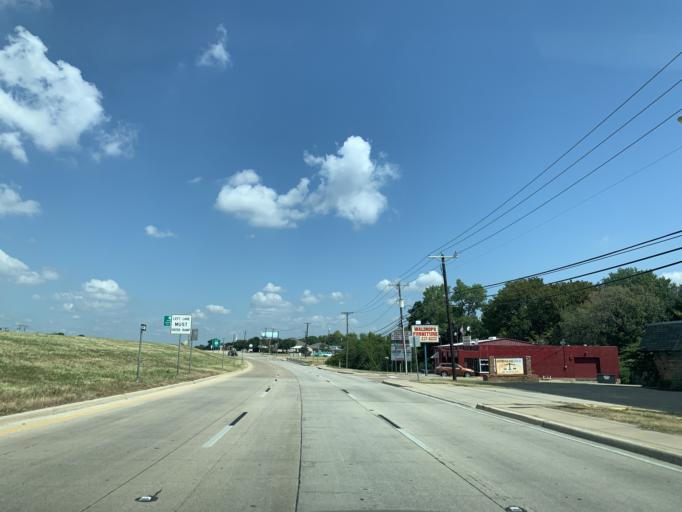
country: US
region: Texas
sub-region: Tarrant County
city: Azle
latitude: 32.8688
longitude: -97.5239
